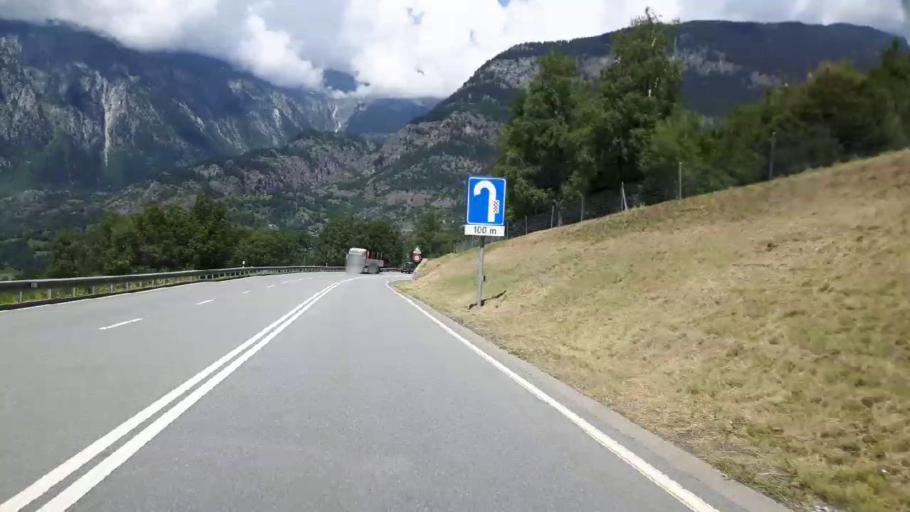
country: CH
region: Valais
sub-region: Brig District
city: Naters
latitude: 46.3270
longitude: 8.0314
